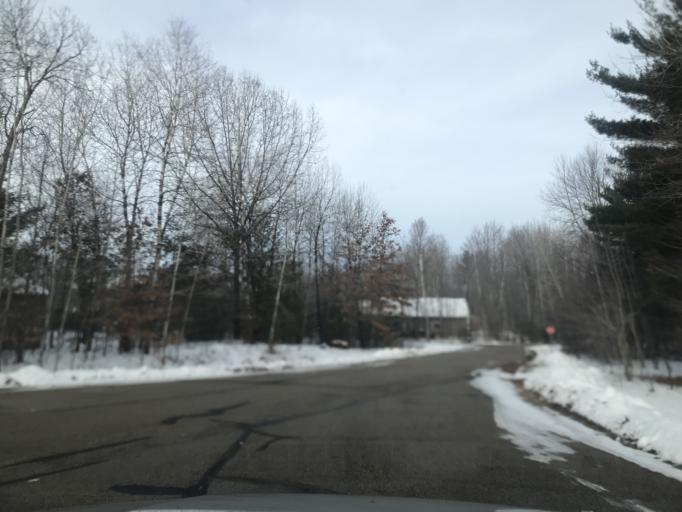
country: US
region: Wisconsin
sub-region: Brown County
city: Suamico
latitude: 44.6893
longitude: -88.0612
